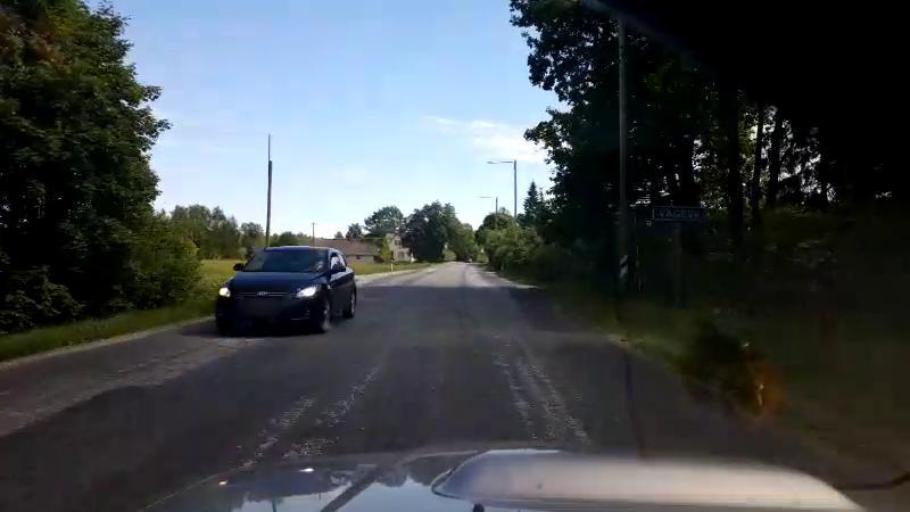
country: EE
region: Laeaene-Virumaa
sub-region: Rakke vald
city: Rakke
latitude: 58.9115
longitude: 26.2738
